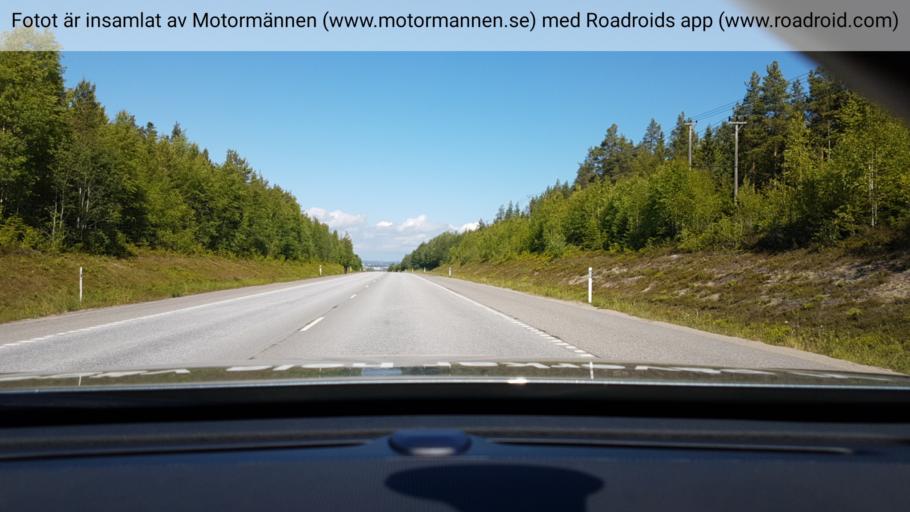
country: SE
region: Vaesterbotten
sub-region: Umea Kommun
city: Holmsund
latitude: 63.7597
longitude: 20.3469
